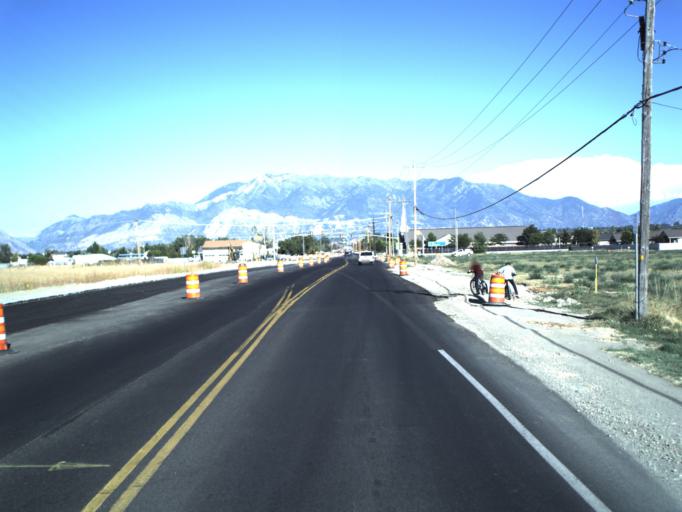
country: US
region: Utah
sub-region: Weber County
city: Hooper
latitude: 41.1907
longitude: -112.0959
